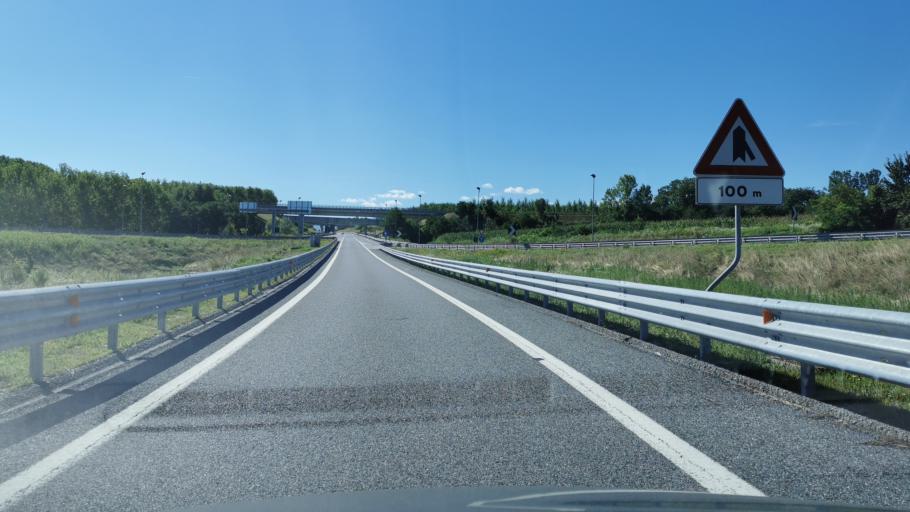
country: IT
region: Piedmont
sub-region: Provincia di Cuneo
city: Cuneo
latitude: 44.4236
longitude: 7.5893
